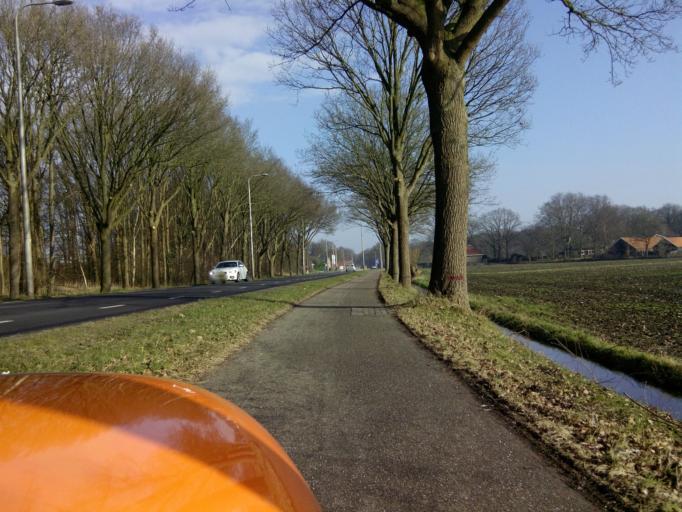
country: NL
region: Utrecht
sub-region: Gemeente Amersfoort
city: Randenbroek
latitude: 52.1825
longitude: 5.4370
